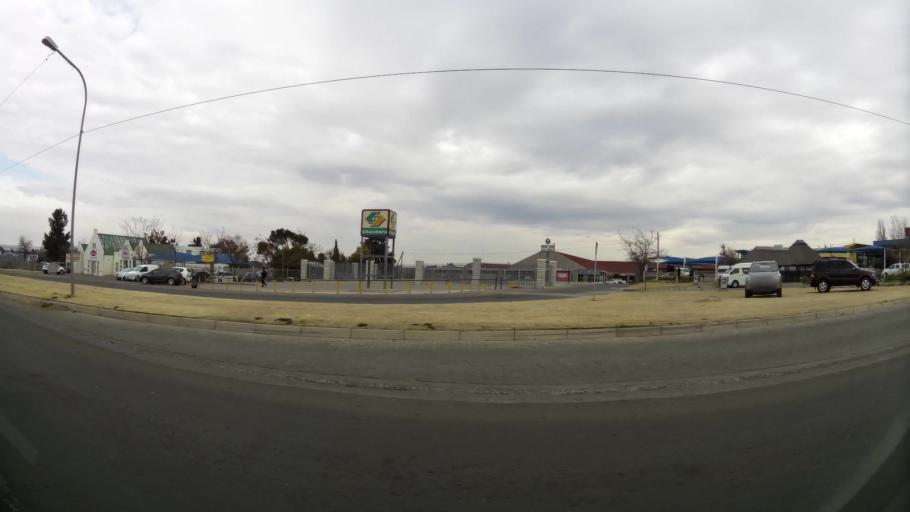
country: ZA
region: Orange Free State
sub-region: Fezile Dabi District Municipality
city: Kroonstad
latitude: -27.6494
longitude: 27.2316
